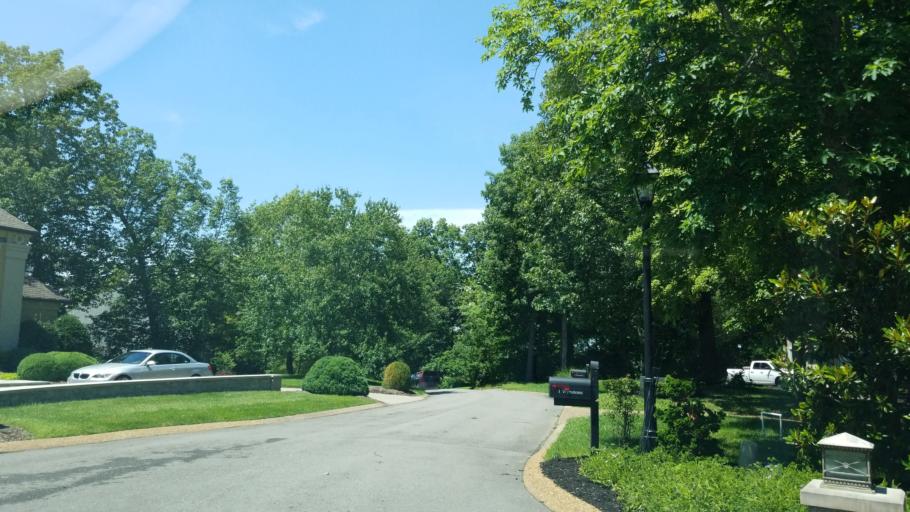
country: US
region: Tennessee
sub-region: Davidson County
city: Forest Hills
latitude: 36.0484
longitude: -86.8266
